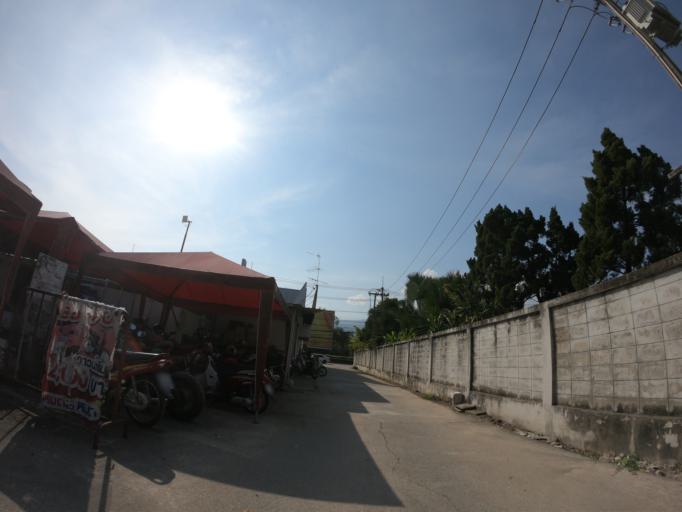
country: TH
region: Chiang Mai
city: Chiang Mai
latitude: 18.8200
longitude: 98.9815
